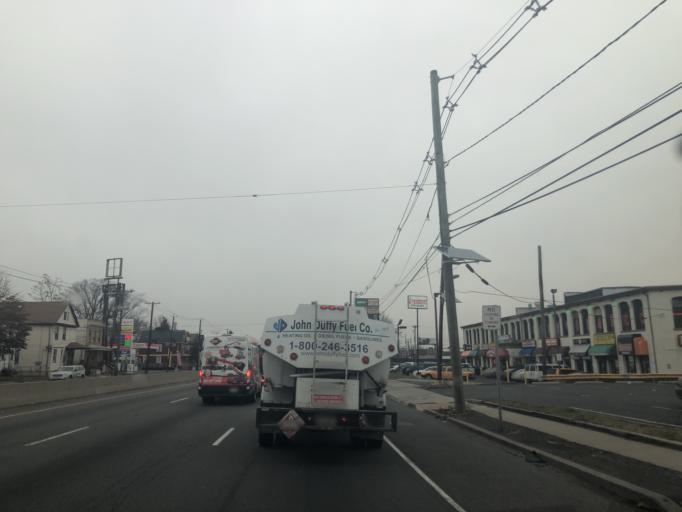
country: US
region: New Jersey
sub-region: Union County
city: Elizabeth
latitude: 40.6752
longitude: -74.1989
